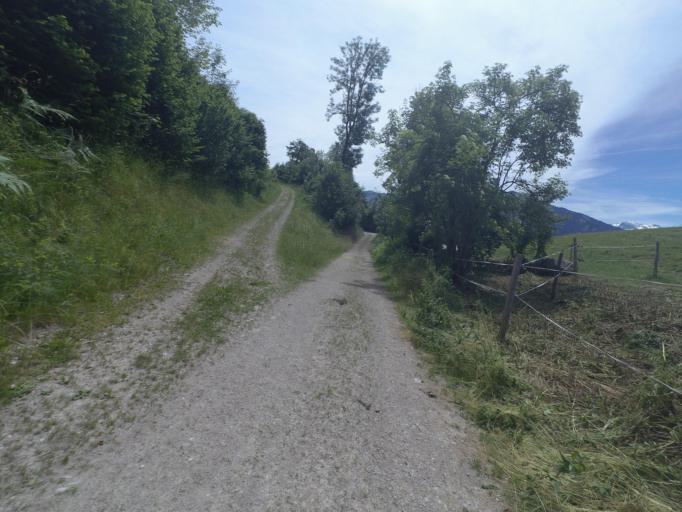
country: AT
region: Salzburg
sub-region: Politischer Bezirk Zell am See
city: Saalfelden am Steinernen Meer
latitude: 47.4405
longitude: 12.8579
